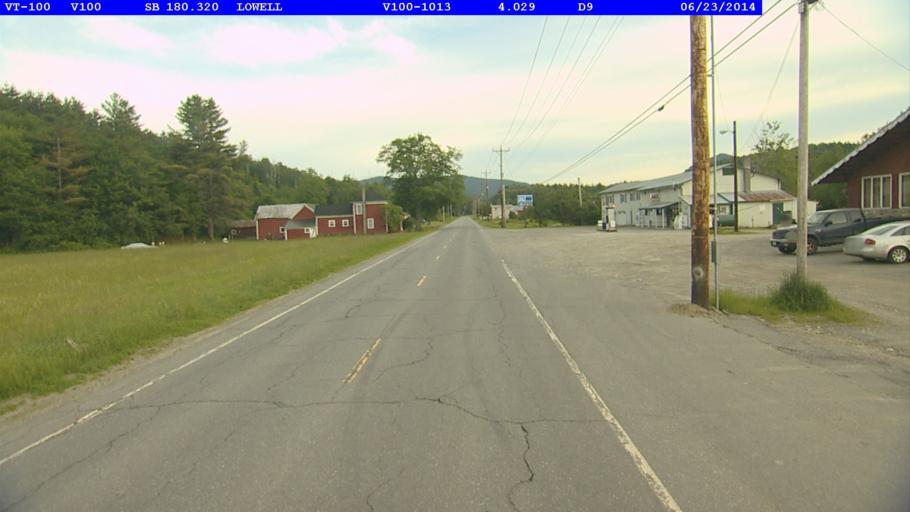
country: US
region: Vermont
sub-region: Lamoille County
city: Hyde Park
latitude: 44.7941
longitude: -72.4482
